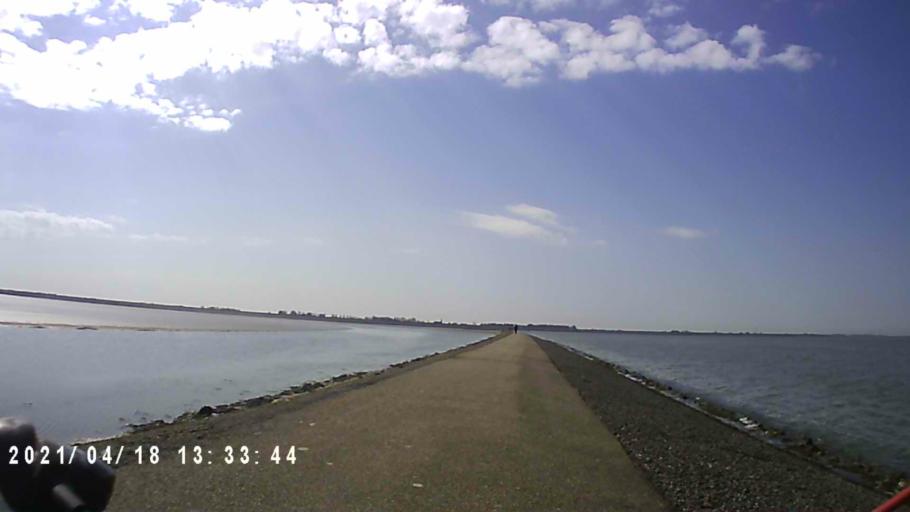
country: NL
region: Friesland
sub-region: Gemeente Dongeradeel
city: Anjum
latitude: 53.4130
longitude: 6.0972
